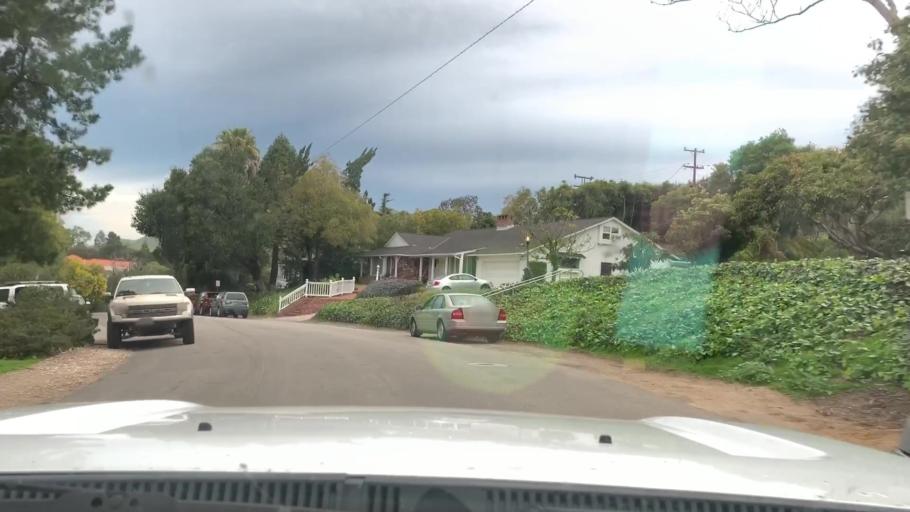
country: US
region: California
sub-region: San Luis Obispo County
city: San Luis Obispo
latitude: 35.2952
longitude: -120.6593
